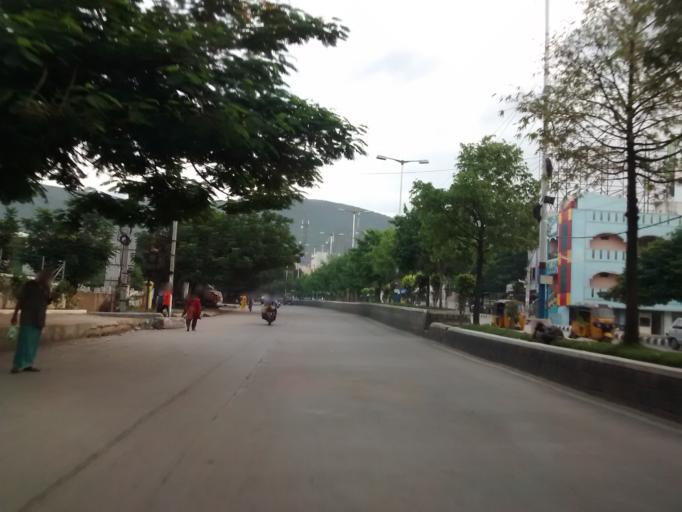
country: IN
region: Andhra Pradesh
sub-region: Chittoor
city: Akkarampalle
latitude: 13.6439
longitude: 79.4275
